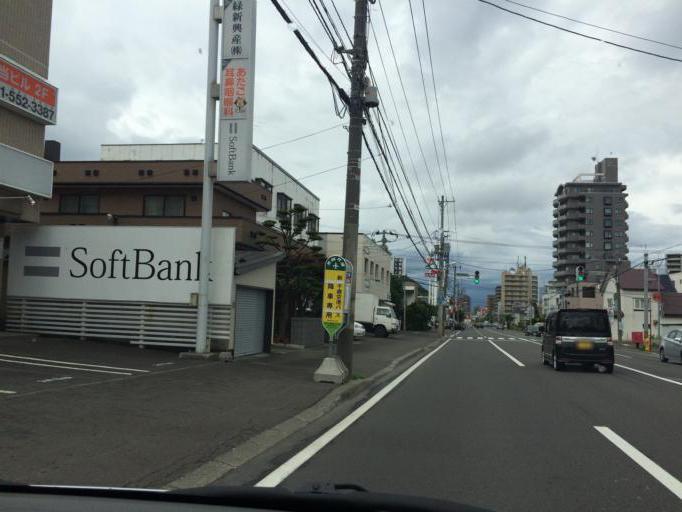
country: JP
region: Hokkaido
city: Sapporo
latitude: 43.0381
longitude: 141.3300
